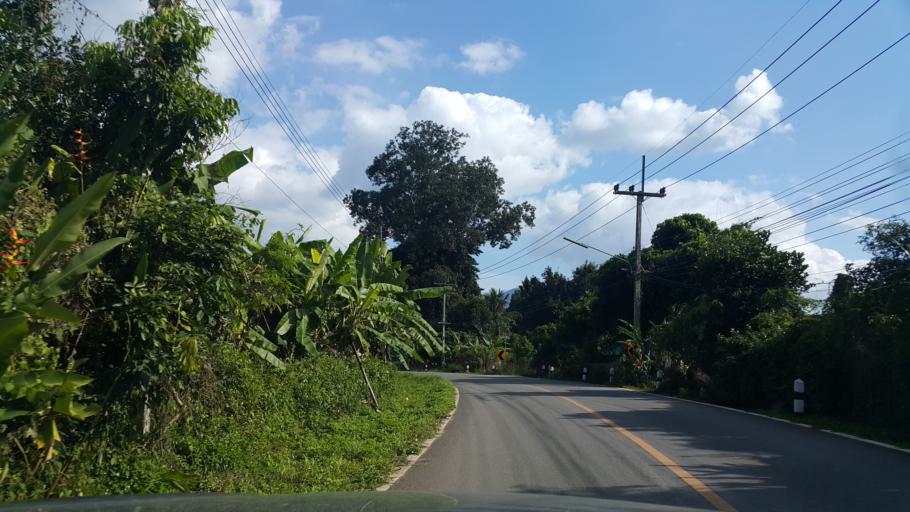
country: TH
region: Lamphun
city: Mae Tha
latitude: 18.5662
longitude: 99.2569
